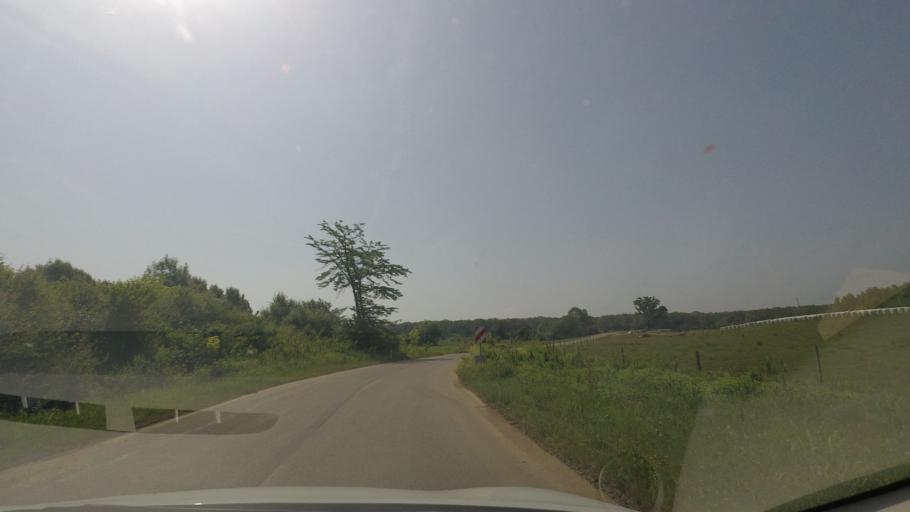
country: HR
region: Karlovacka
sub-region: Grad Karlovac
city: Karlovac
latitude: 45.4860
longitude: 15.5898
